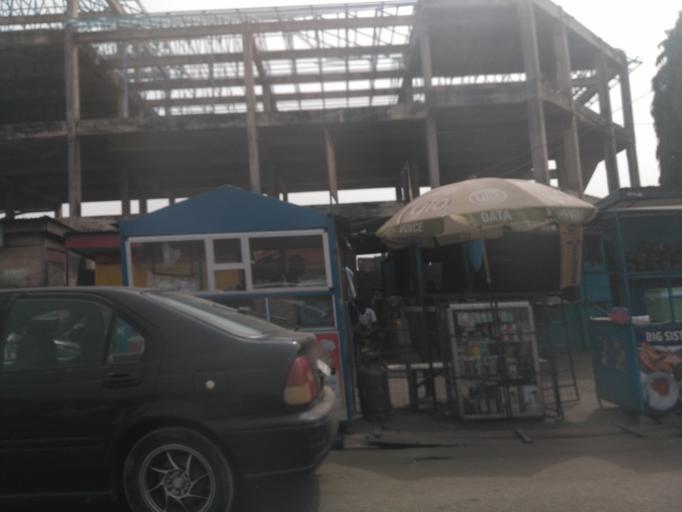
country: GH
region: Ashanti
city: Tafo
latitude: 6.7137
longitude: -1.6147
